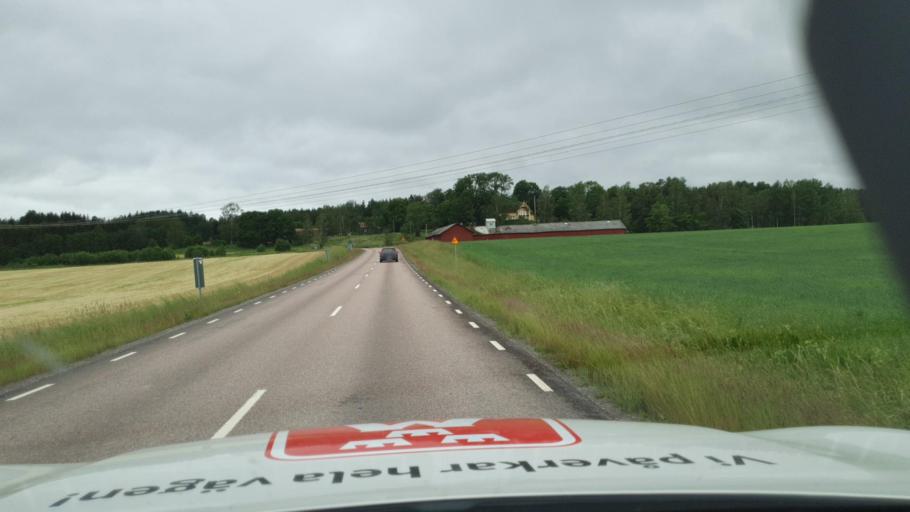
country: SE
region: Vaermland
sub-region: Karlstads Kommun
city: Edsvalla
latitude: 59.4199
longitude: 13.2107
